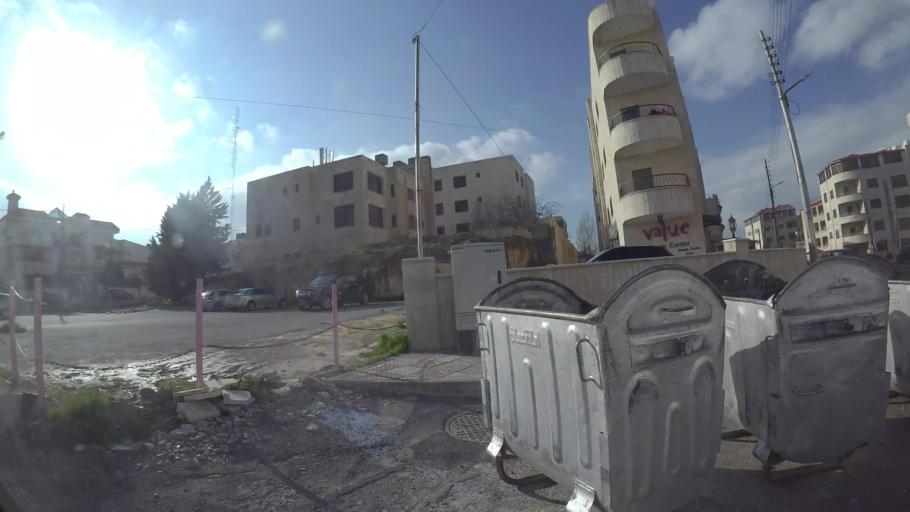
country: JO
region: Amman
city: Al Jubayhah
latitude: 32.0111
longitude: 35.8631
